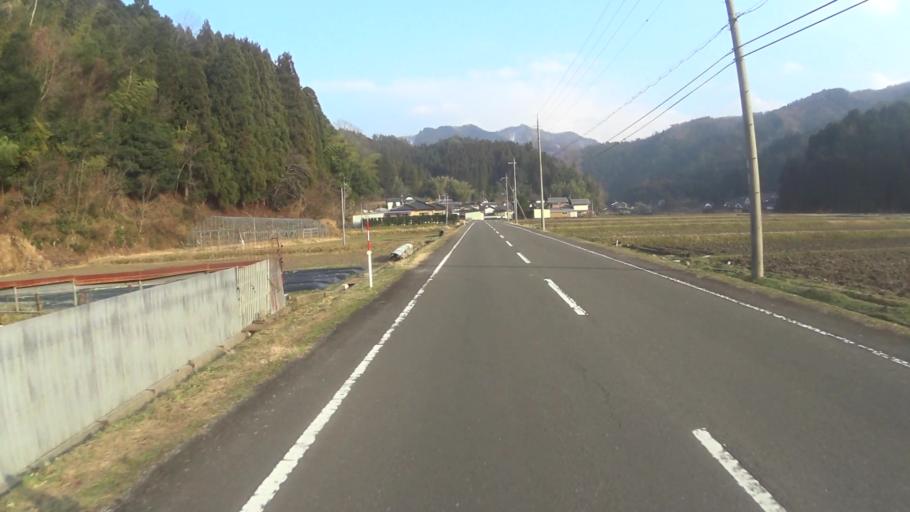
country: JP
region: Kyoto
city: Maizuru
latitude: 35.3698
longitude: 135.4502
